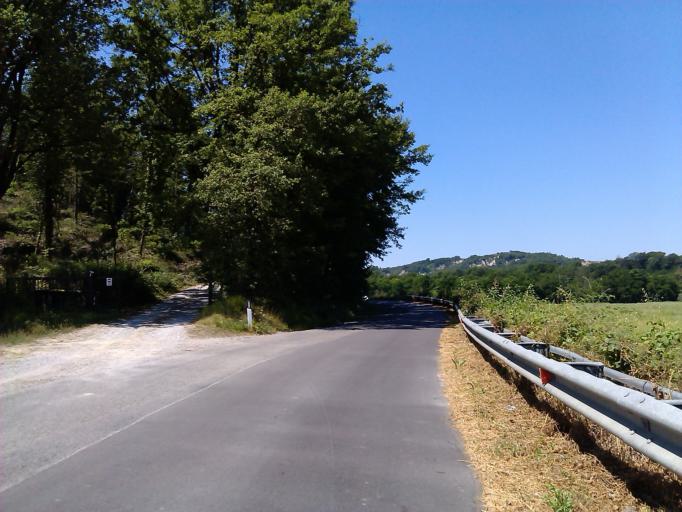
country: IT
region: Umbria
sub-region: Provincia di Terni
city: Fabro Scalo
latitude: 42.8593
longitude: 12.0454
